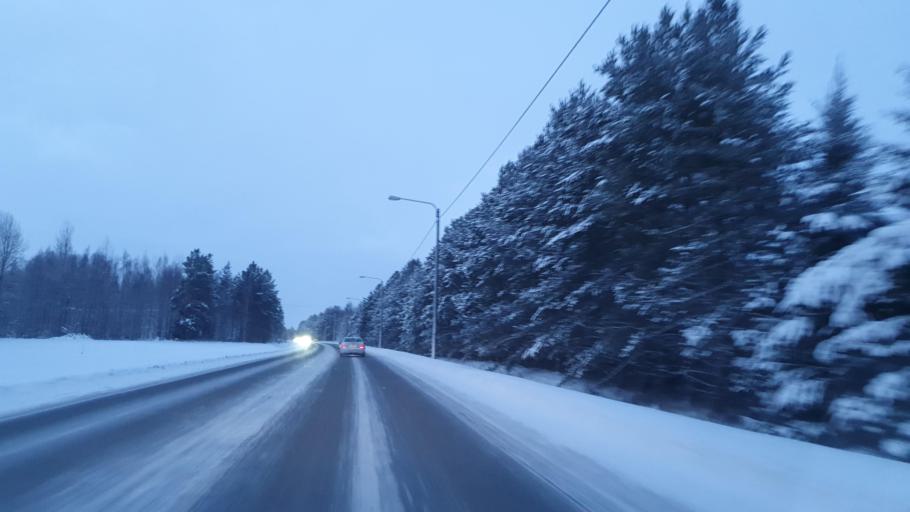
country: FI
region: Northern Ostrobothnia
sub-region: Oulu
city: Muhos
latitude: 64.8639
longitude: 25.8846
